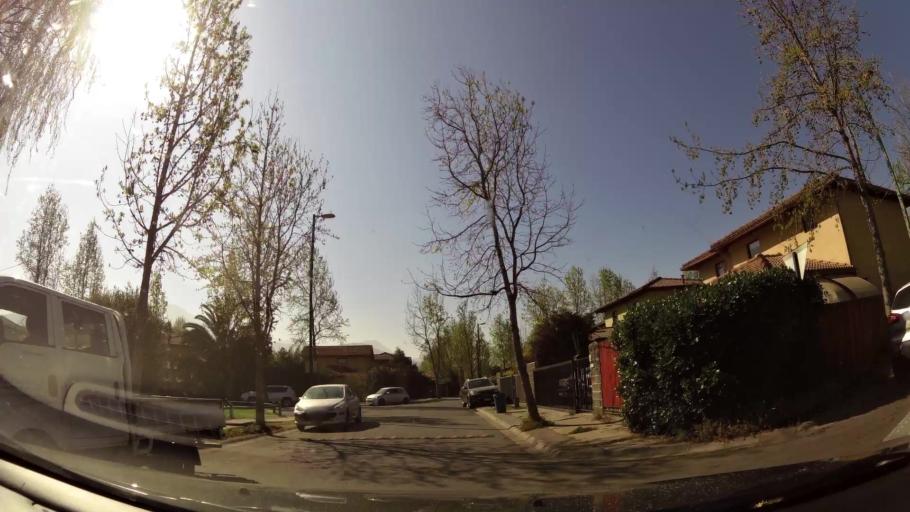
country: CL
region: Santiago Metropolitan
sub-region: Provincia de Chacabuco
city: Chicureo Abajo
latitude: -33.3581
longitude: -70.6813
